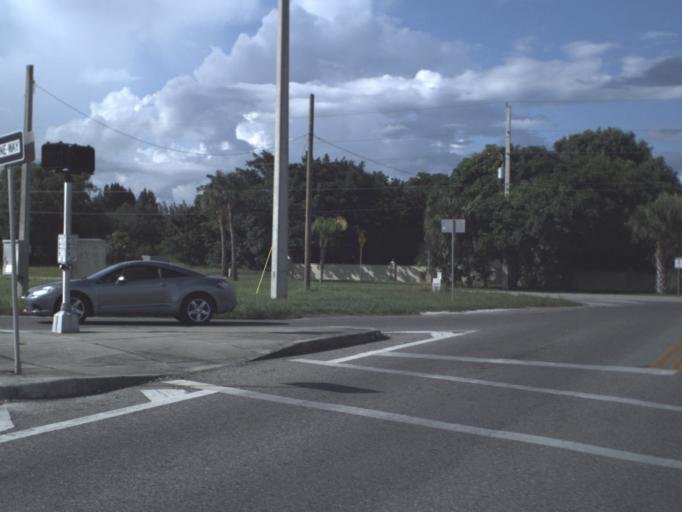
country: US
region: Florida
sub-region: Charlotte County
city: Punta Gorda
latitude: 26.9425
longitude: -82.0324
